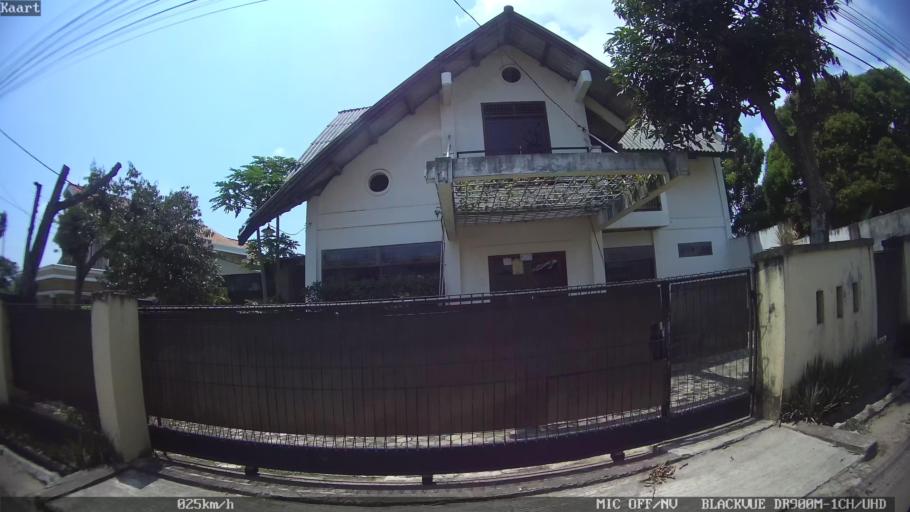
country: ID
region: Lampung
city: Kedaton
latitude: -5.3624
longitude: 105.2693
